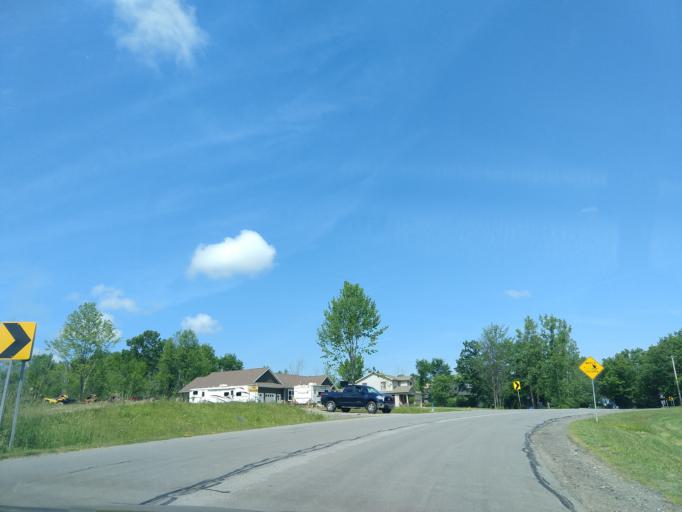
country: US
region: New York
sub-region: Erie County
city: East Aurora
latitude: 42.7581
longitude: -78.6260
